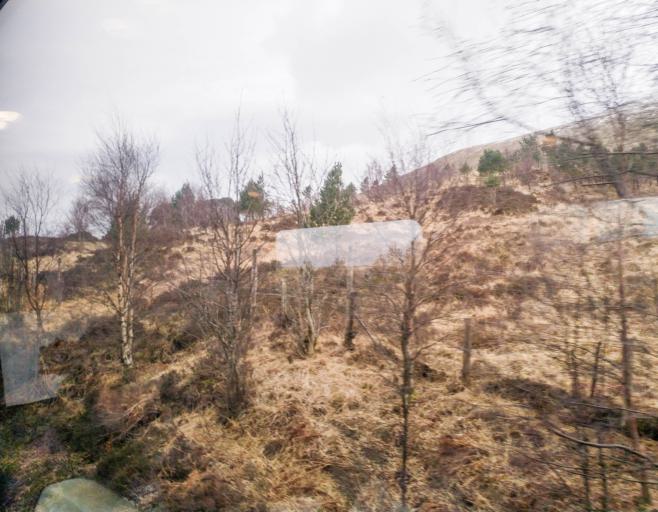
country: GB
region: Scotland
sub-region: Highland
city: Spean Bridge
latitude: 56.5693
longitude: -4.6950
